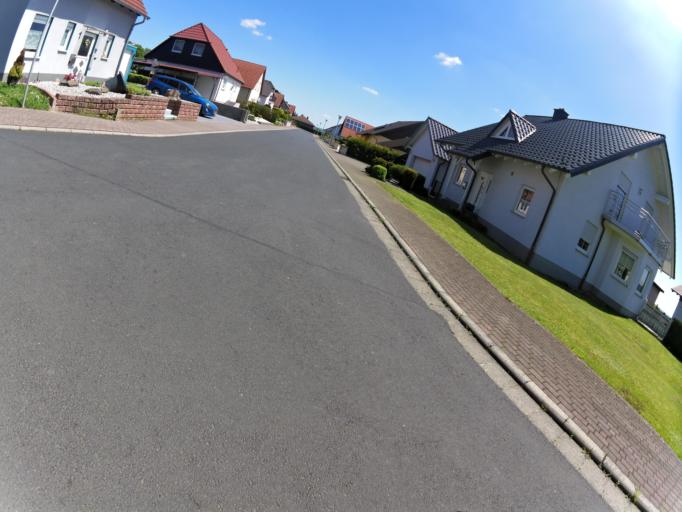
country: DE
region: Thuringia
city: Dankmarshausen
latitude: 50.9527
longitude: 9.9982
